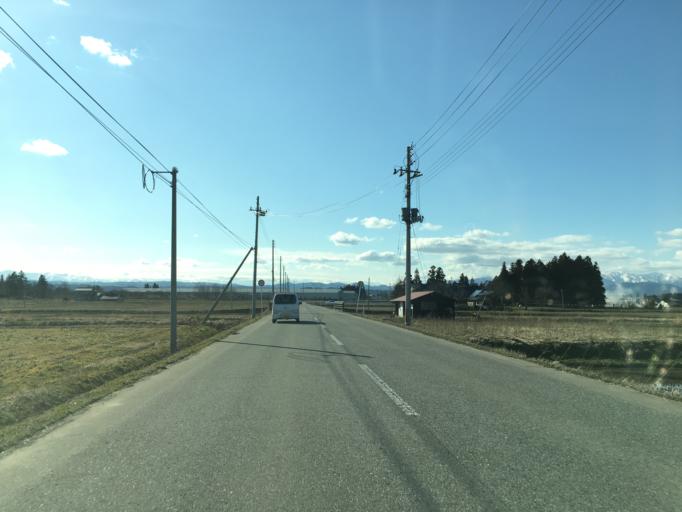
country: JP
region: Yamagata
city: Takahata
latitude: 38.0068
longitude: 140.0966
